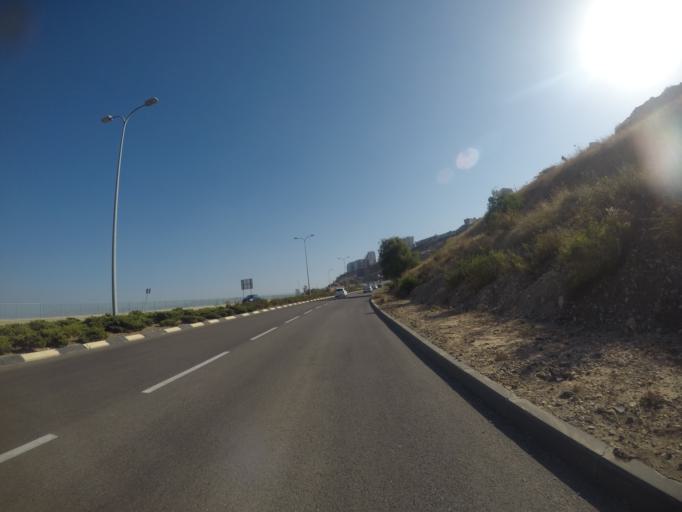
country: IL
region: Northern District
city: Tiberias
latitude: 32.8032
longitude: 35.5301
